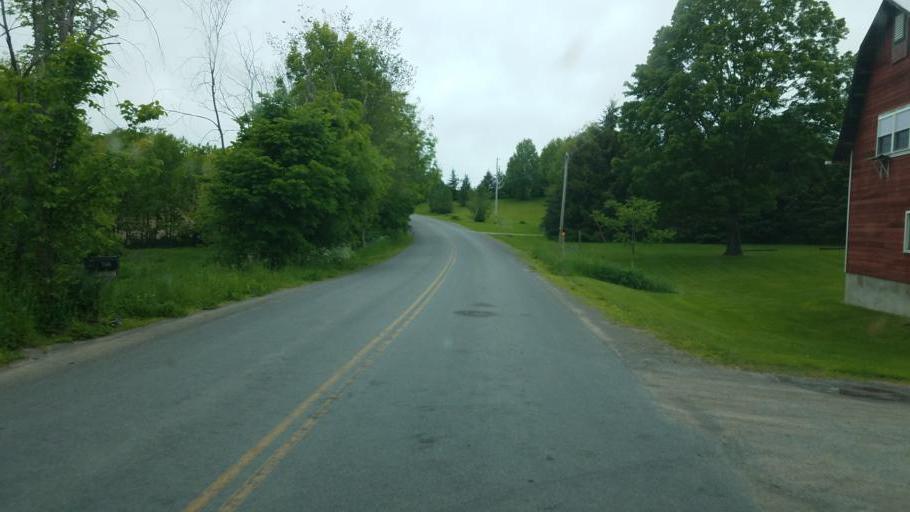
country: US
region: New York
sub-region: Oneida County
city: Chadwicks
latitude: 42.9192
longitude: -75.2182
